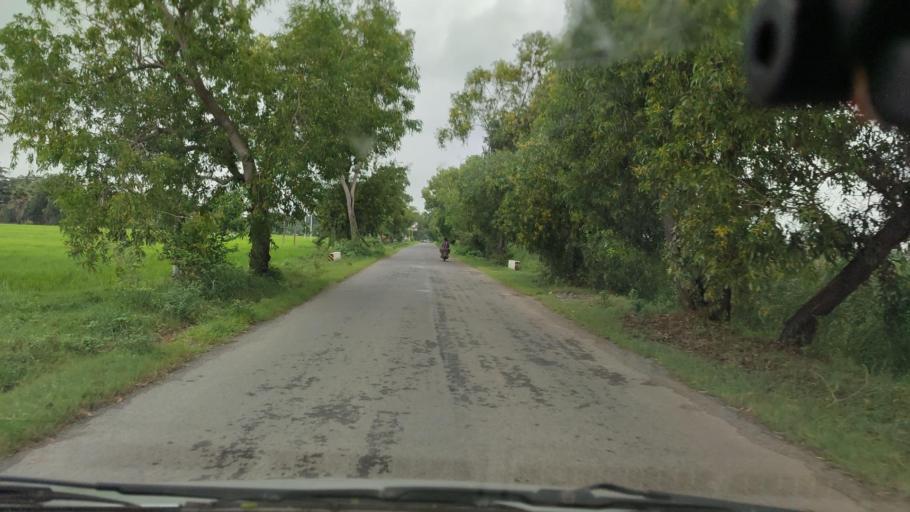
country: MM
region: Bago
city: Pyay
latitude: 18.8689
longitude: 95.4212
